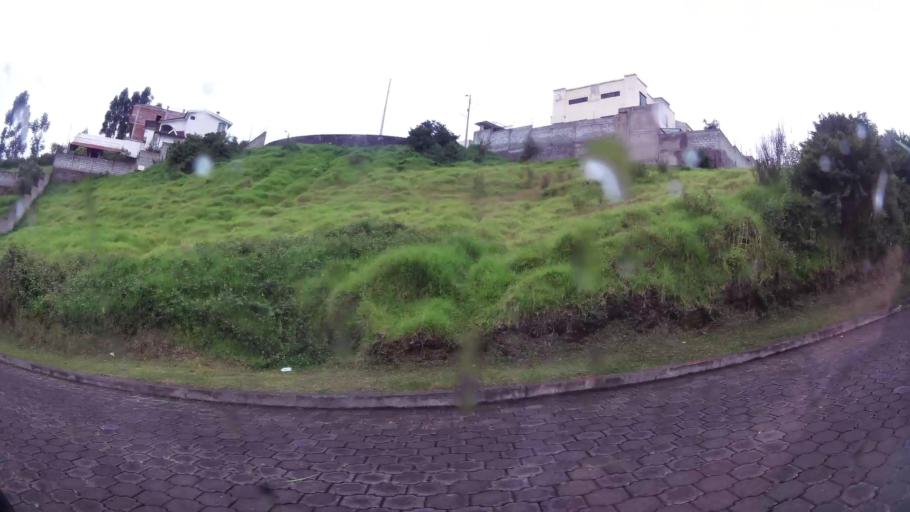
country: EC
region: Pichincha
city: Sangolqui
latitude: -0.3213
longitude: -78.4379
